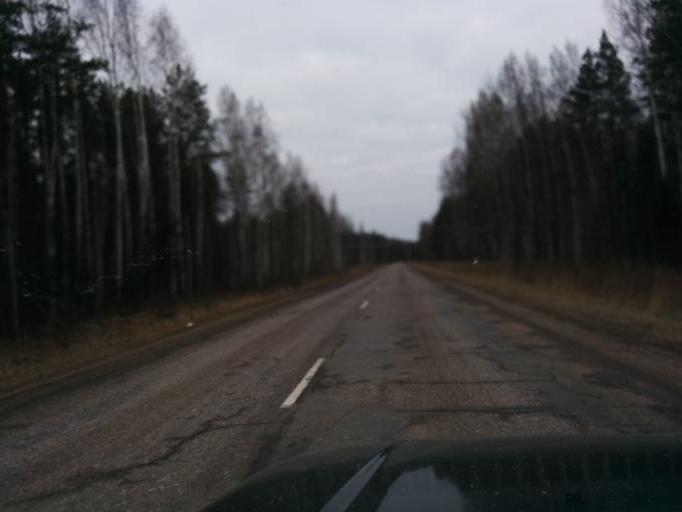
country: LV
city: Tireli
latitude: 56.9133
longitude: 23.5260
